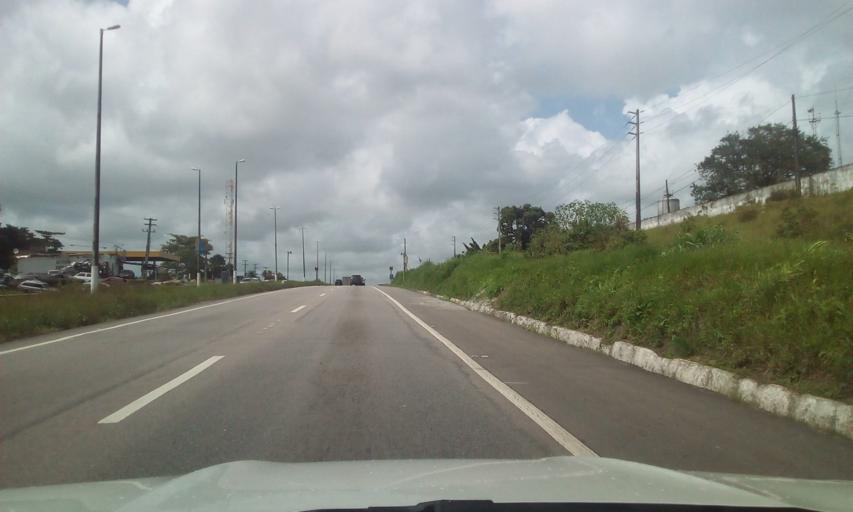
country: BR
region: Pernambuco
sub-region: Igarassu
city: Igarassu
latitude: -7.8184
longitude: -34.9170
